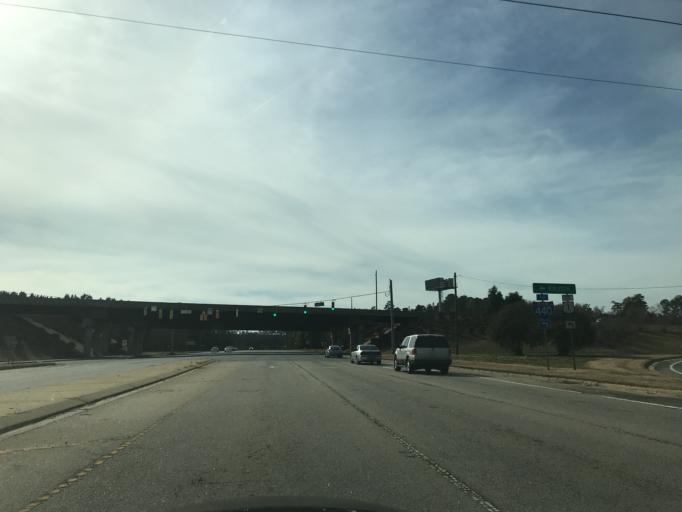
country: US
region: North Carolina
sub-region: Wake County
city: Cary
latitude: 35.8084
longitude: -78.7222
